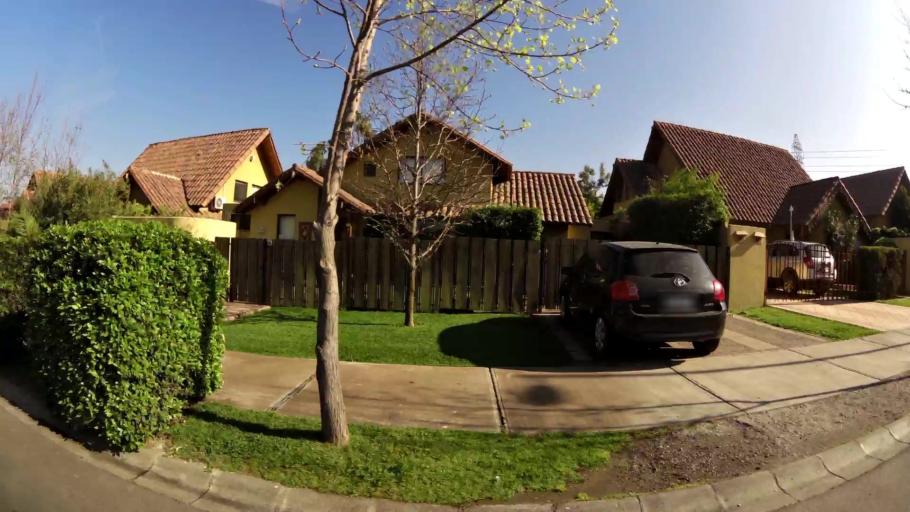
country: CL
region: Santiago Metropolitan
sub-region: Provincia de Chacabuco
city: Chicureo Abajo
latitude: -33.3491
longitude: -70.6678
